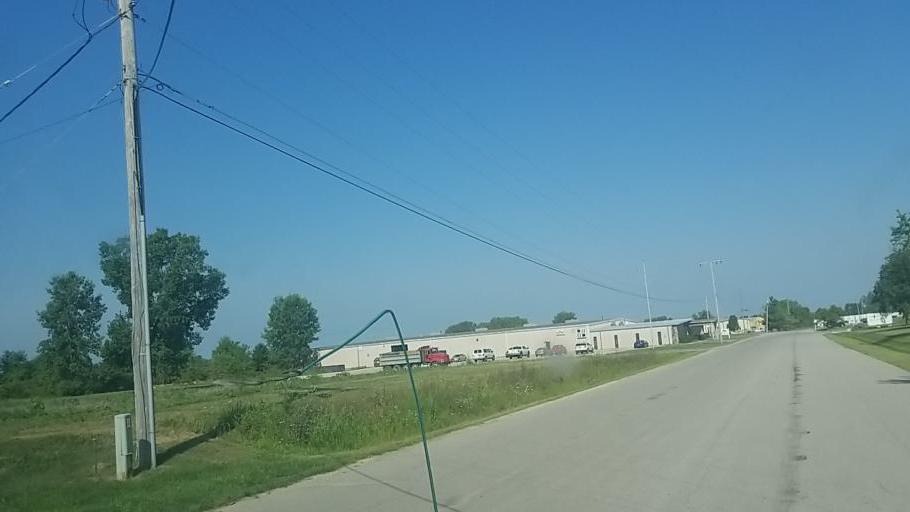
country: US
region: Ohio
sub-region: Marion County
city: Marion
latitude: 40.6170
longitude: -83.0896
